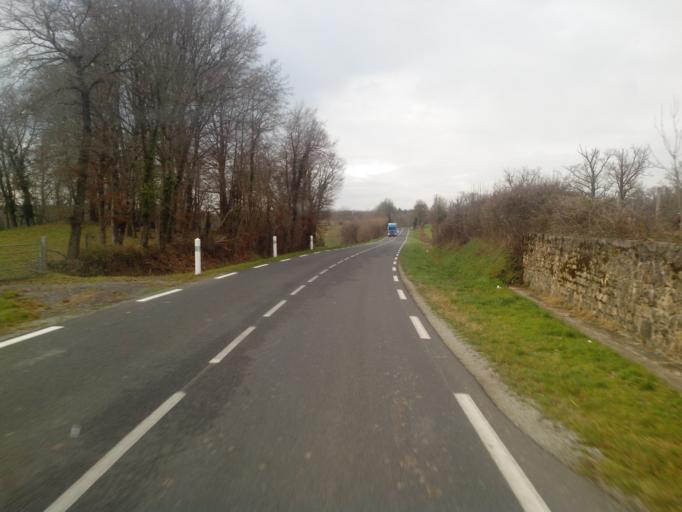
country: FR
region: Limousin
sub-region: Departement de la Haute-Vienne
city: Magnac-Laval
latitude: 46.2143
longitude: 1.1326
